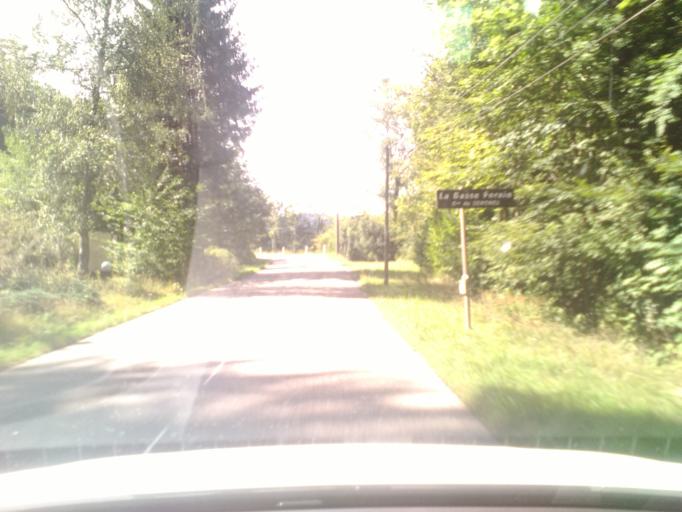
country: FR
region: Lorraine
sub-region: Departement des Vosges
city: Senones
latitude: 48.3900
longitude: 6.9691
